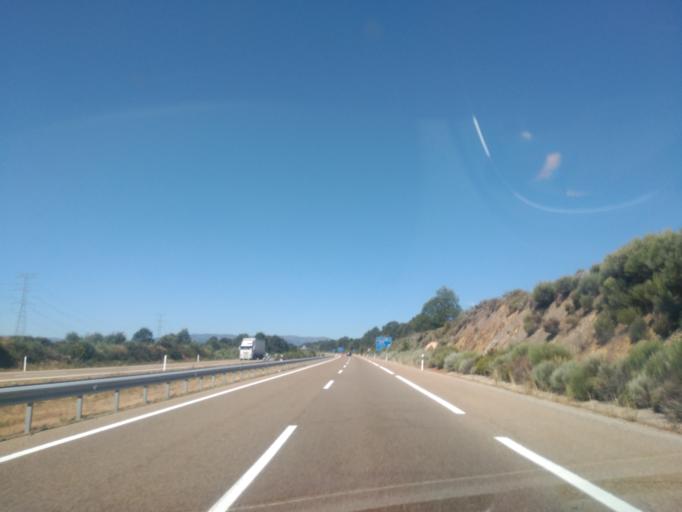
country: ES
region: Castille and Leon
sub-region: Provincia de Zamora
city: Palacios de Sanabria
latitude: 42.0498
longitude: -6.5338
